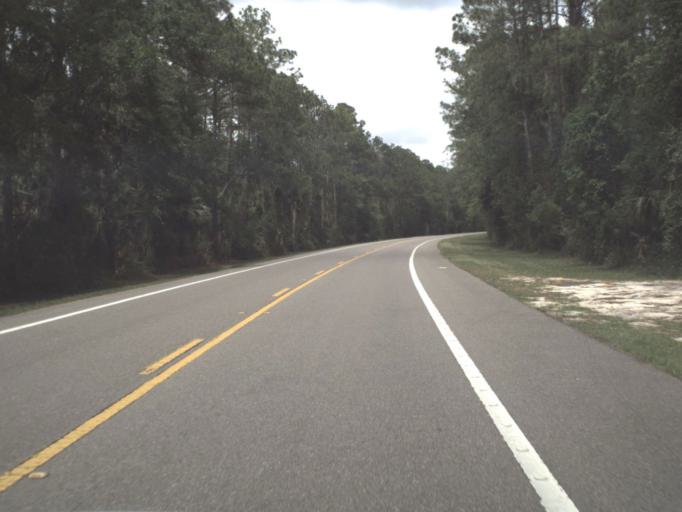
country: US
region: Florida
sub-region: Flagler County
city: Bunnell
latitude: 29.4240
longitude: -81.2985
